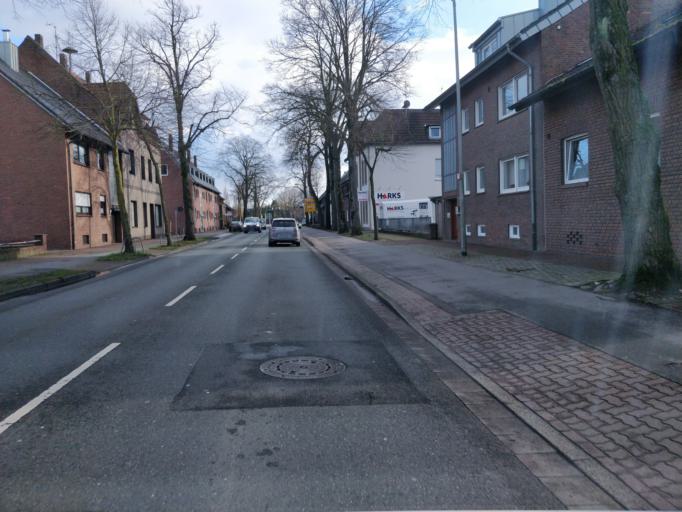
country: DE
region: North Rhine-Westphalia
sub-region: Regierungsbezirk Dusseldorf
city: Bocholt
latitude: 51.8481
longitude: 6.5987
